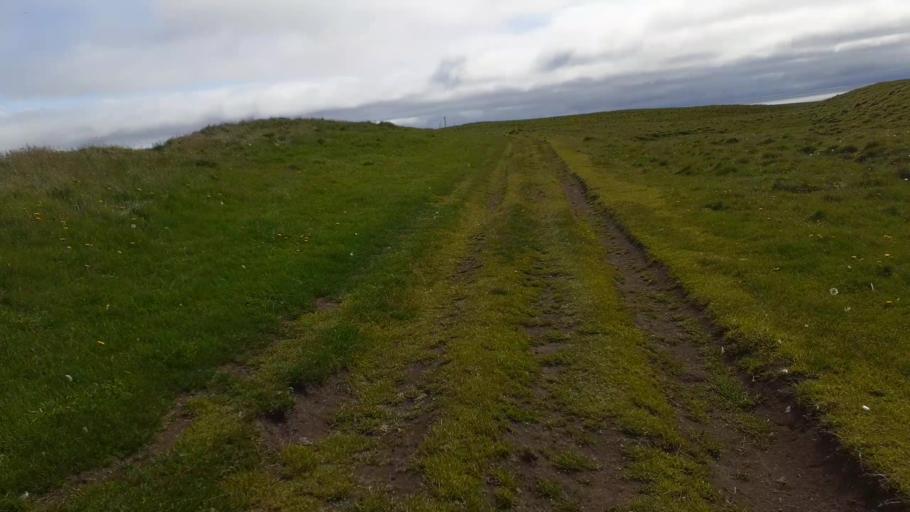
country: IS
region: Northeast
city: Dalvik
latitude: 66.5555
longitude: -18.0021
